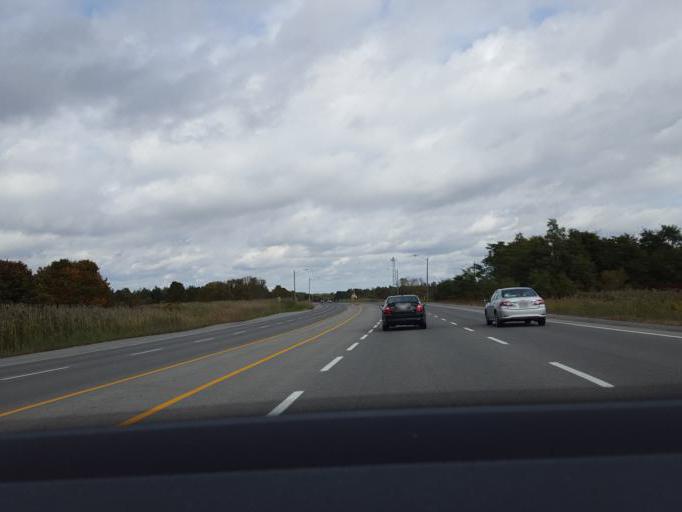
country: CA
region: Ontario
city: Pickering
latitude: 43.8625
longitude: -79.1477
